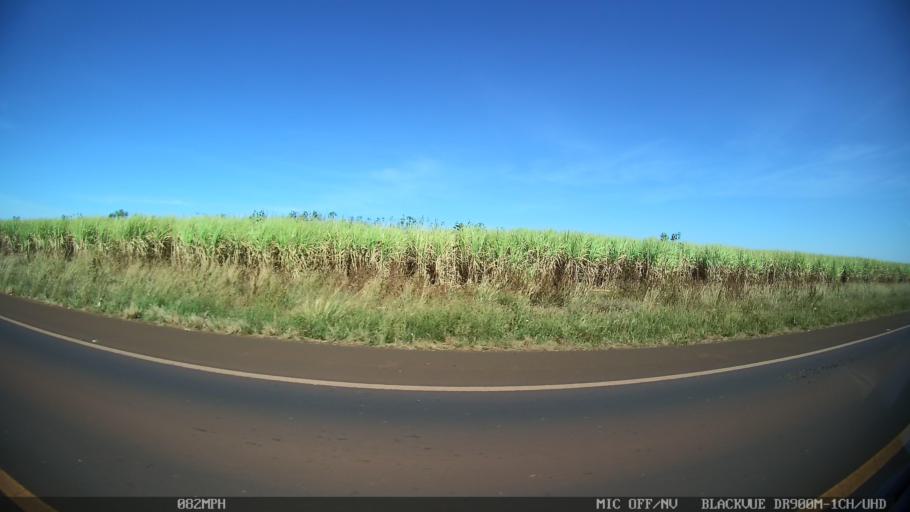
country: BR
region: Sao Paulo
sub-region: Guaira
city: Guaira
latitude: -20.4440
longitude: -48.3541
